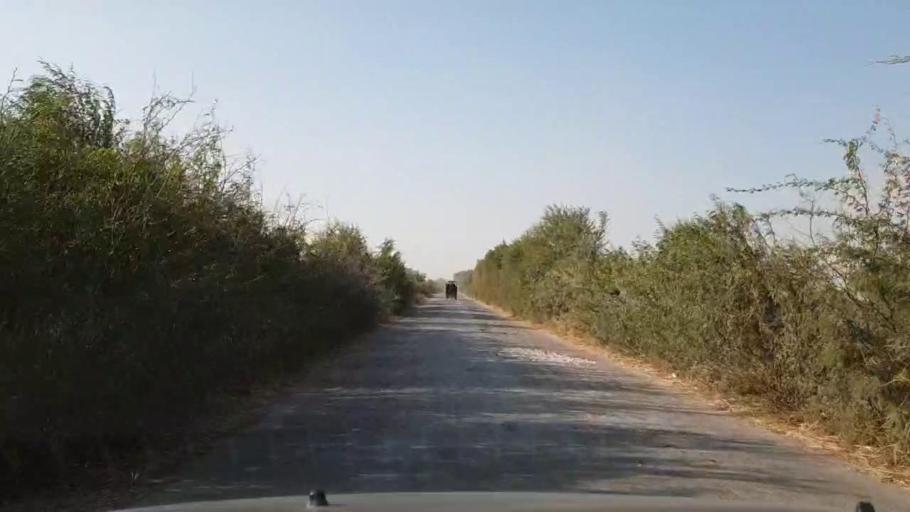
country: PK
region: Sindh
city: Tando Ghulam Ali
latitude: 25.1523
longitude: 68.8579
